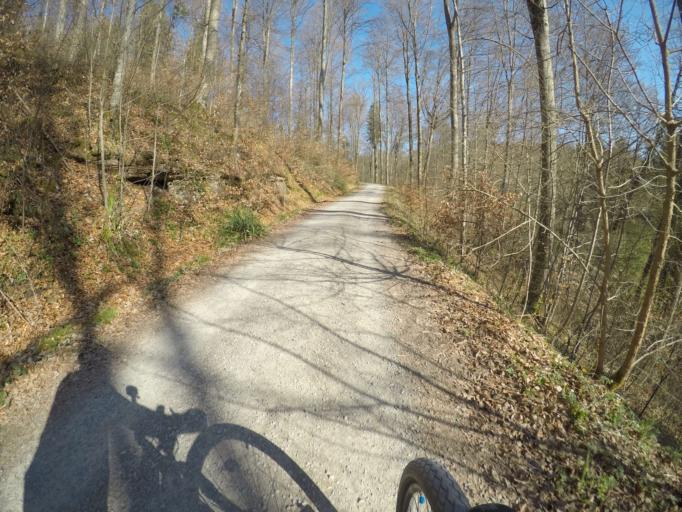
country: DE
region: Baden-Wuerttemberg
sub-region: Tuebingen Region
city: Dettenhausen
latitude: 48.6046
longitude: 9.1093
